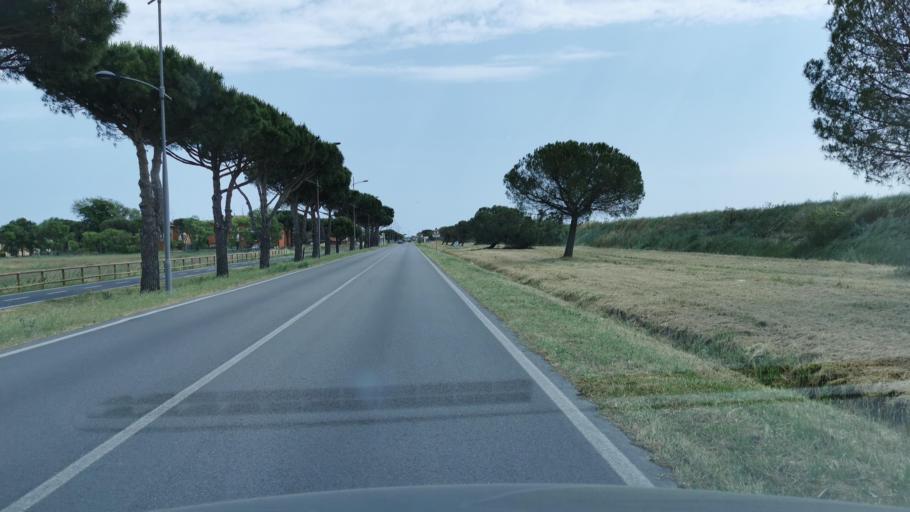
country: IT
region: Emilia-Romagna
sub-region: Provincia di Ferrara
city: Comacchio
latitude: 44.6879
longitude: 12.1909
